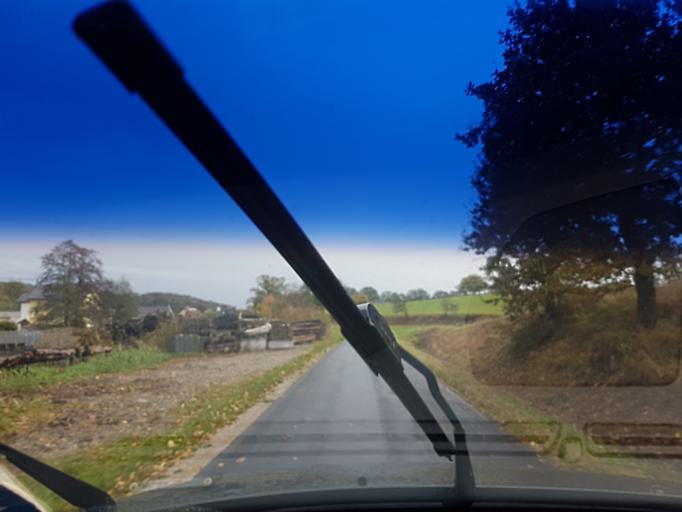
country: DE
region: Bavaria
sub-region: Regierungsbezirk Mittelfranken
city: Wachenroth
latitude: 49.7602
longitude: 10.6862
